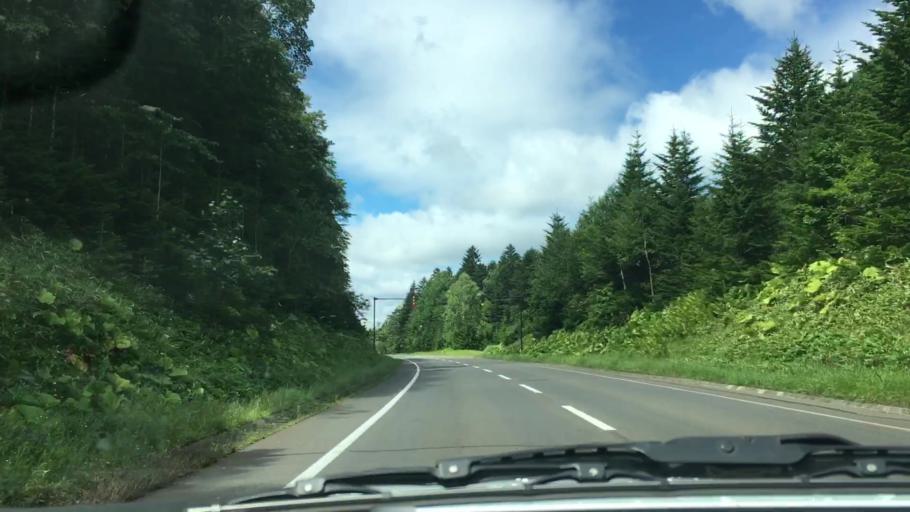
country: JP
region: Hokkaido
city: Bihoro
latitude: 43.4411
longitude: 144.0487
